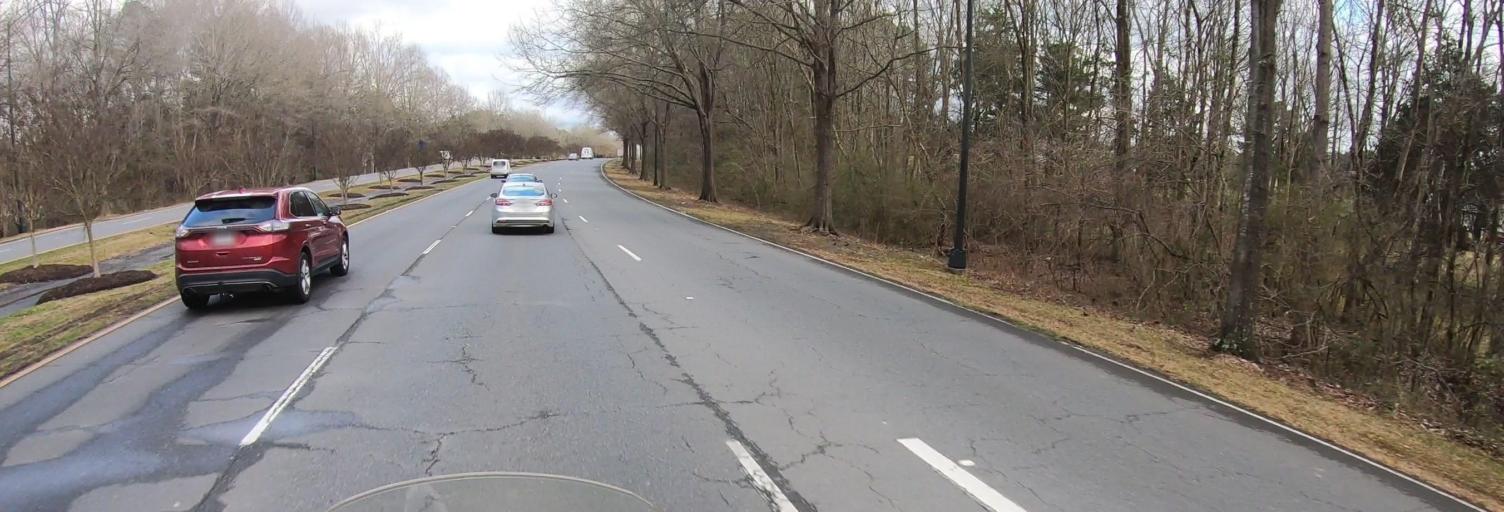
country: US
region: South Carolina
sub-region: York County
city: Rock Hill
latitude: 34.9407
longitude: -80.9934
